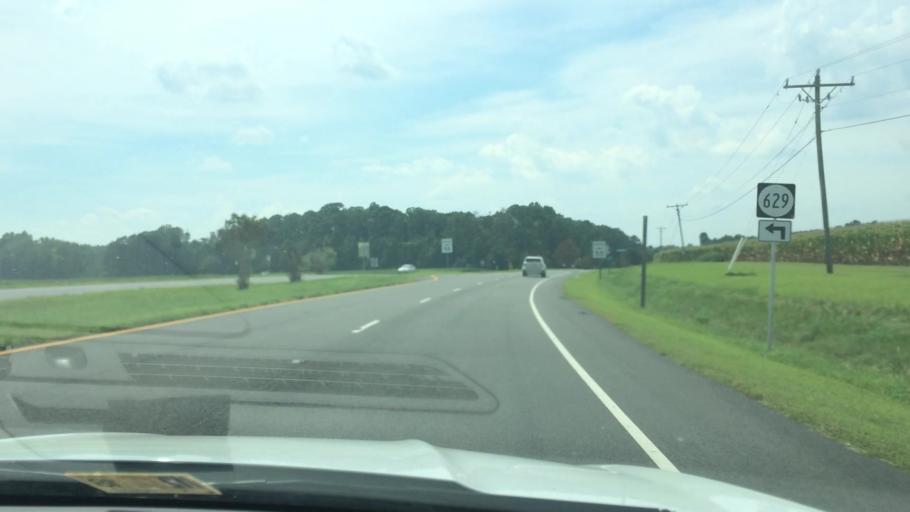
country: US
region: Virginia
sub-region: Middlesex County
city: Saluda
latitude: 37.5992
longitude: -76.5705
